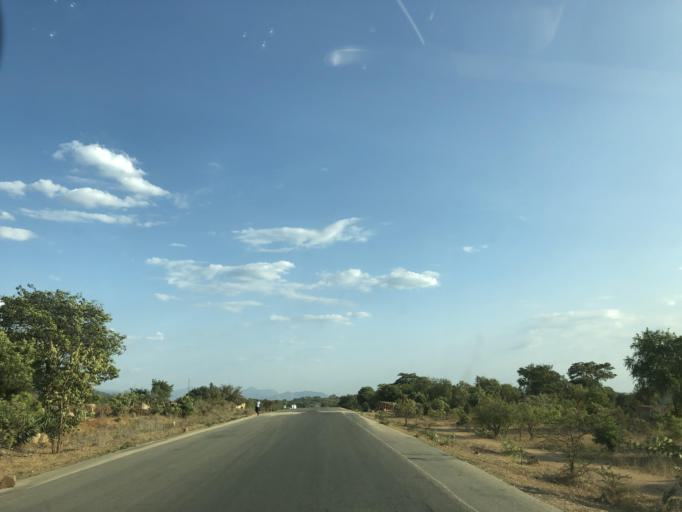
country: AO
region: Huila
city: Caluquembe
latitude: -13.5153
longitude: 13.9219
